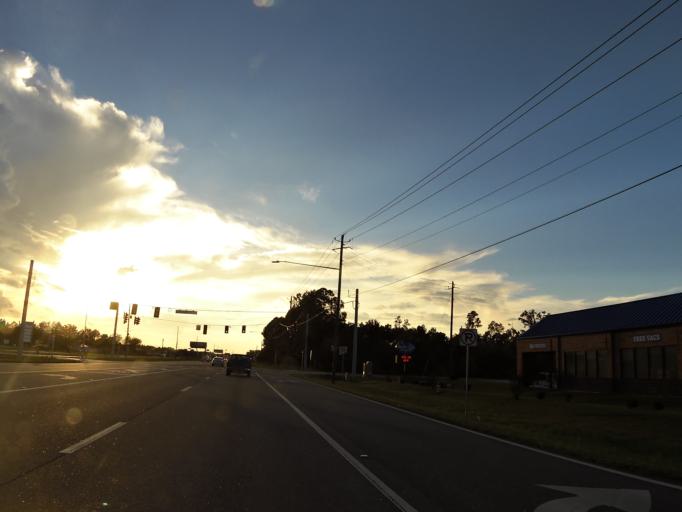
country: US
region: Georgia
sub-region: Camden County
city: Kingsland
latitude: 30.7840
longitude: -81.6375
